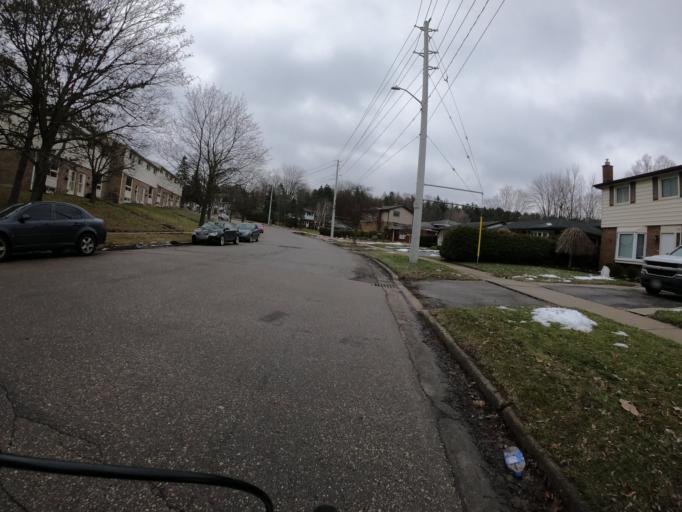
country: CA
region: Ontario
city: Kitchener
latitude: 43.3953
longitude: -80.4277
